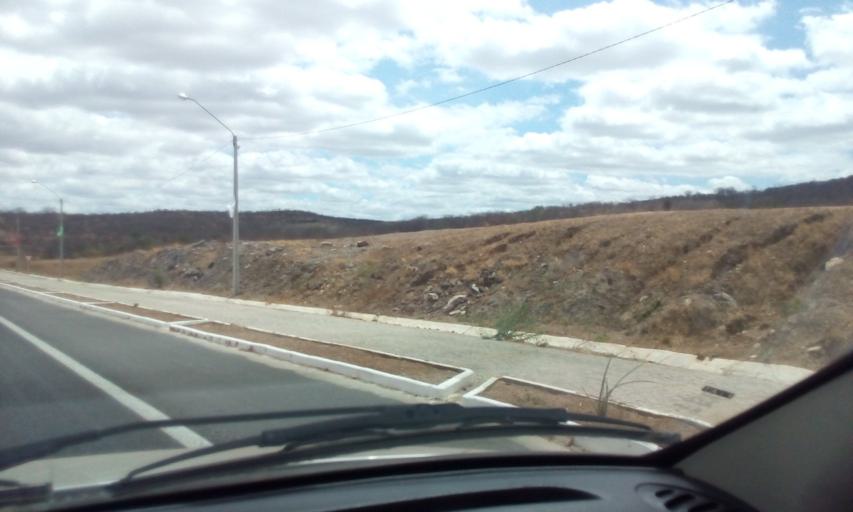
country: BR
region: Rio Grande do Norte
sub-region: Currais Novos
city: Currais Novos
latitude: -6.2571
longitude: -36.4934
